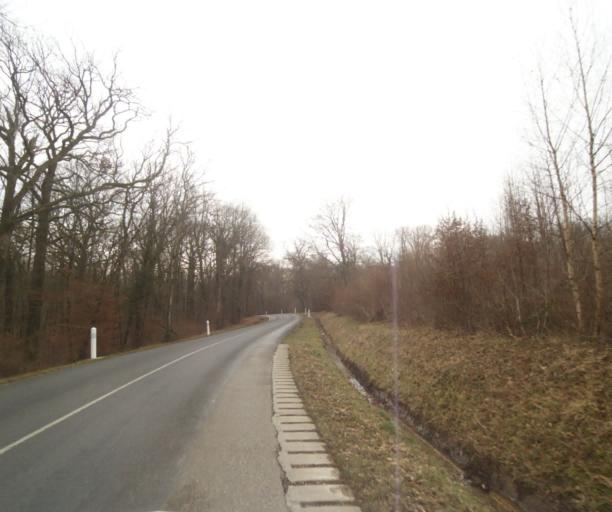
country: FR
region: Champagne-Ardenne
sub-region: Departement de la Marne
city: Pargny-sur-Saulx
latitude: 48.7297
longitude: 4.8664
